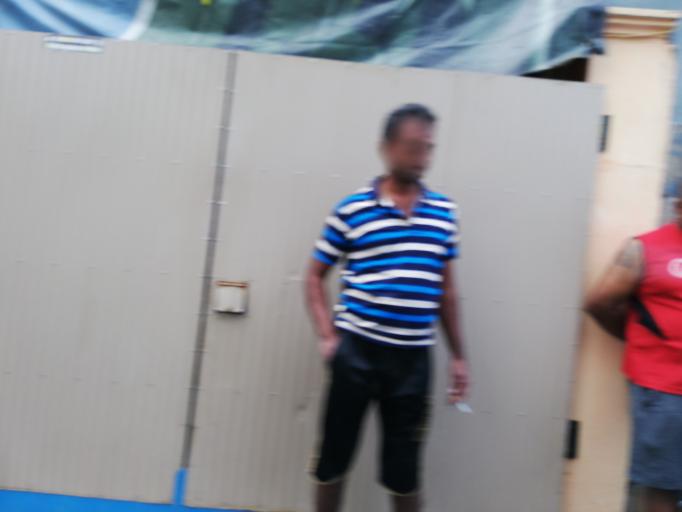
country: MU
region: Plaines Wilhems
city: Ebene
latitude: -20.2330
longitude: 57.4602
